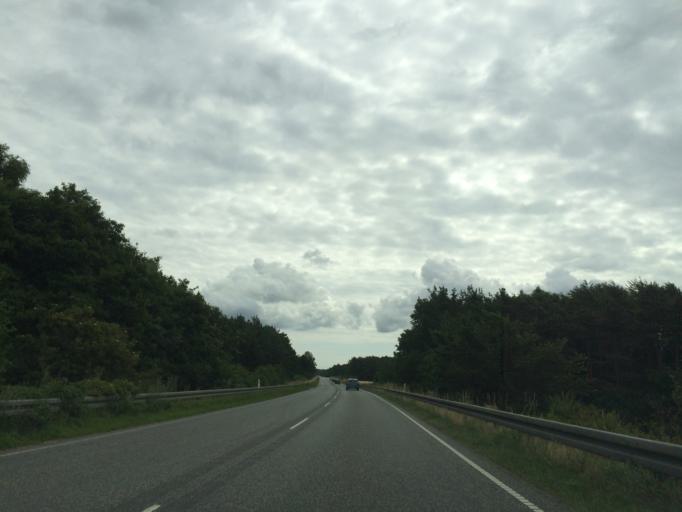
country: DK
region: Central Jutland
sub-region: Syddjurs Kommune
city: Ronde
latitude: 56.2941
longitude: 10.5802
